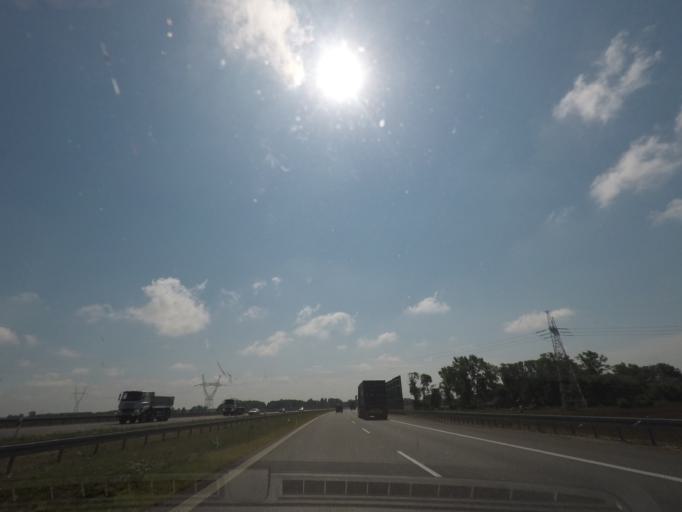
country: PL
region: Kujawsko-Pomorskie
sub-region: Powiat wloclawski
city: Baruchowo
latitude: 52.4364
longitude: 19.2471
